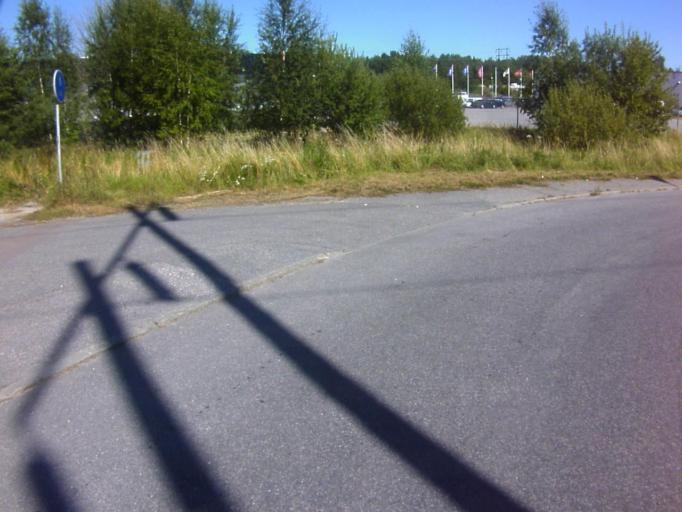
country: SE
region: Soedermanland
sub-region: Eskilstuna Kommun
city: Eskilstuna
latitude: 59.3873
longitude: 16.5010
